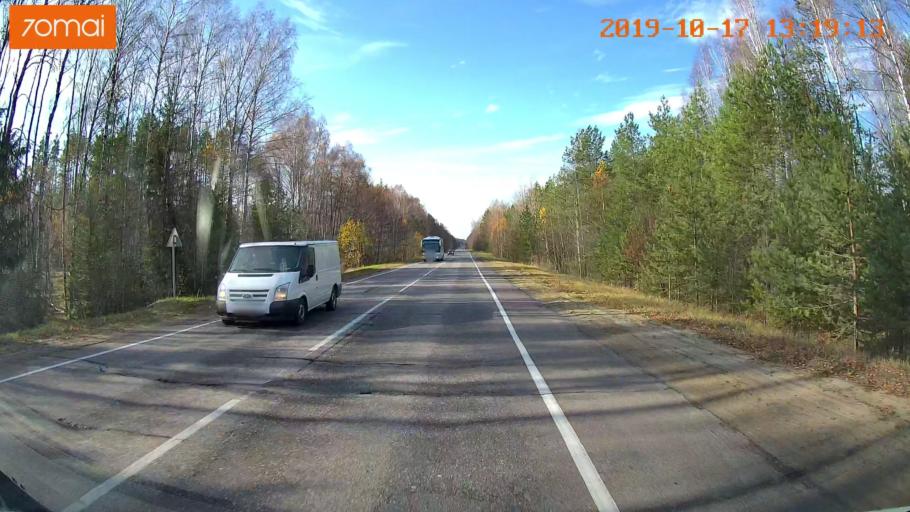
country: RU
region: Rjazan
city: Gus'-Zheleznyy
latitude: 55.0680
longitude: 41.0793
